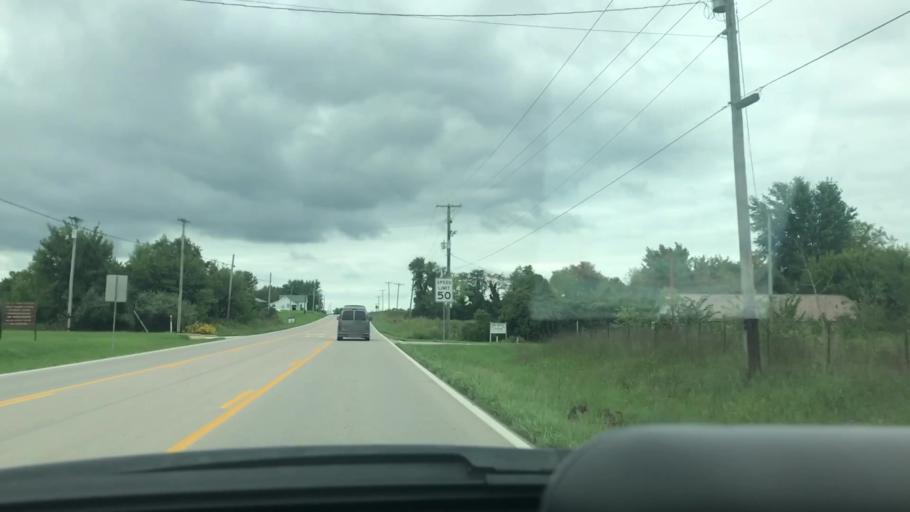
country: US
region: Missouri
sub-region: Dallas County
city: Buffalo
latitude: 37.6491
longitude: -93.1039
